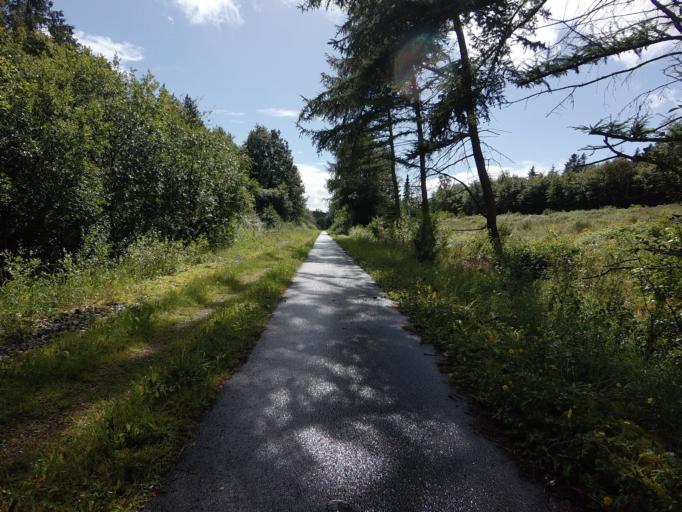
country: DK
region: Central Jutland
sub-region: Silkeborg Kommune
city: Virklund
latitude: 56.1090
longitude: 9.4129
